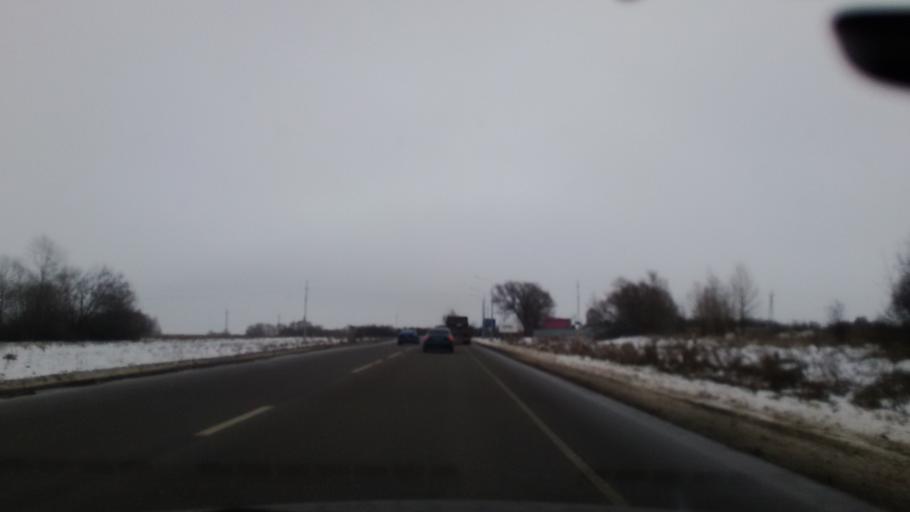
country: RU
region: Tula
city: Borodinskiy
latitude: 54.0289
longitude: 37.8862
